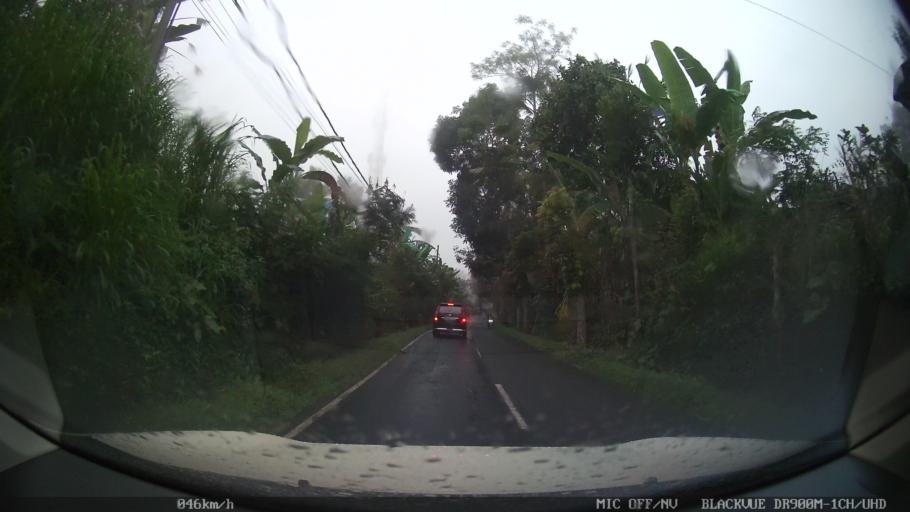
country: ID
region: Bali
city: Banjar Taro Kelod
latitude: -8.3465
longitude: 115.2793
